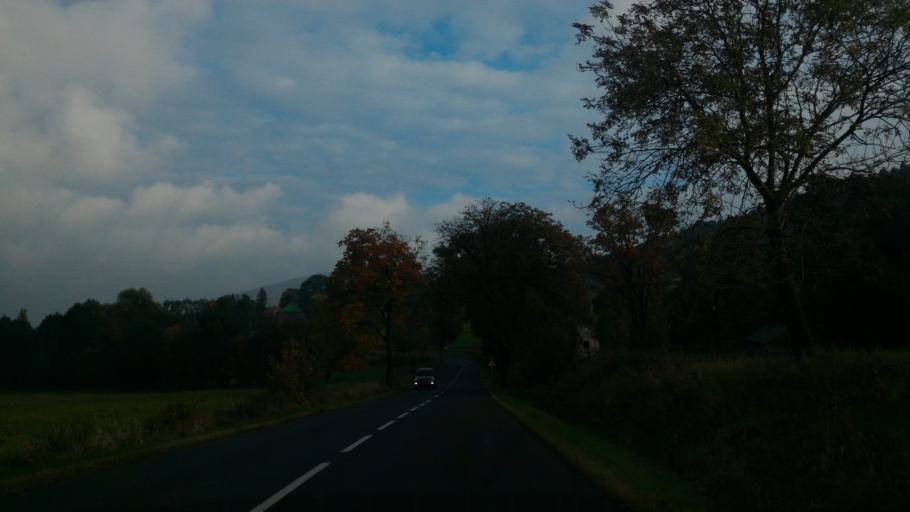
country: CZ
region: Ustecky
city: Dolni Podluzi
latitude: 50.8766
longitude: 14.5635
